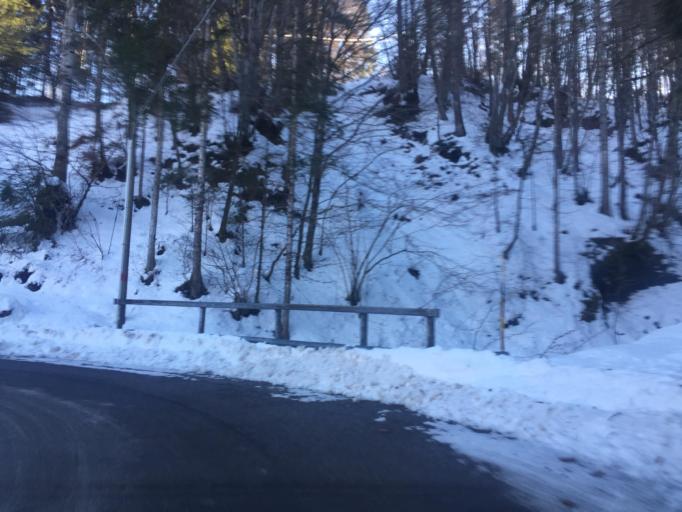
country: IT
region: Friuli Venezia Giulia
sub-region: Provincia di Udine
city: Lauco
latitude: 46.4377
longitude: 12.9470
